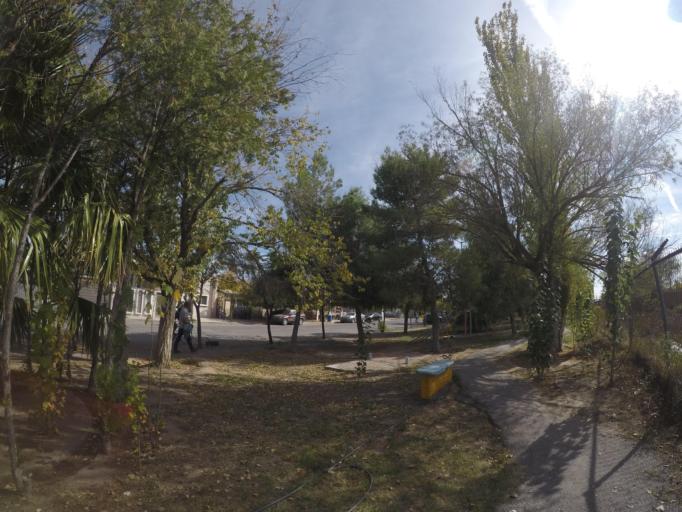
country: MX
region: Chihuahua
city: Ciudad Juarez
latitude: 31.7339
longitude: -106.4354
